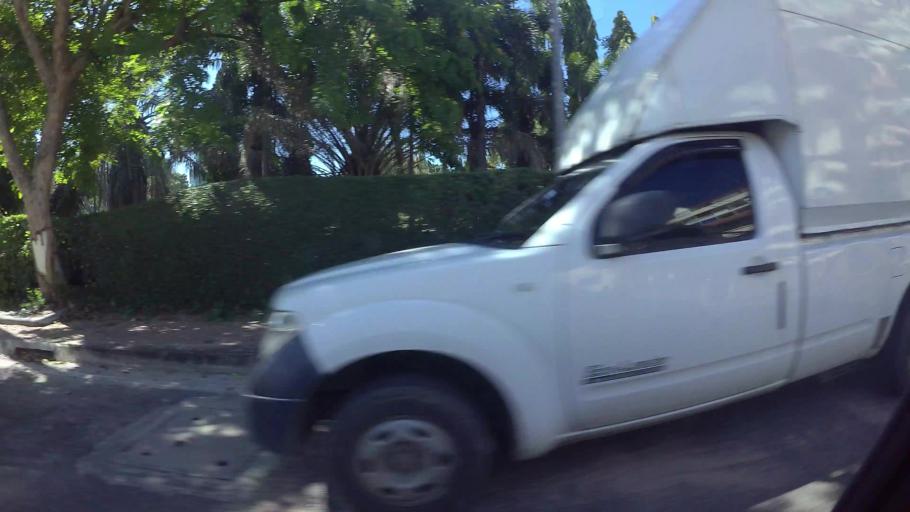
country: TH
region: Chon Buri
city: Phatthaya
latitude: 12.9128
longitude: 100.8607
